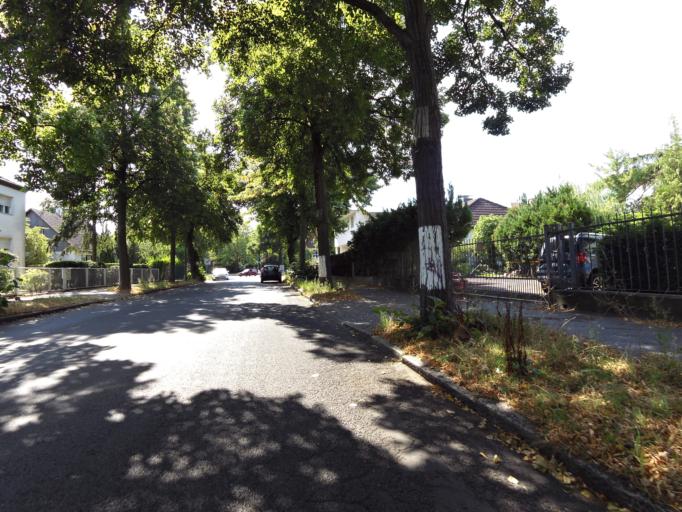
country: DE
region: Berlin
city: Marienfelde
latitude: 52.4284
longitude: 13.3648
